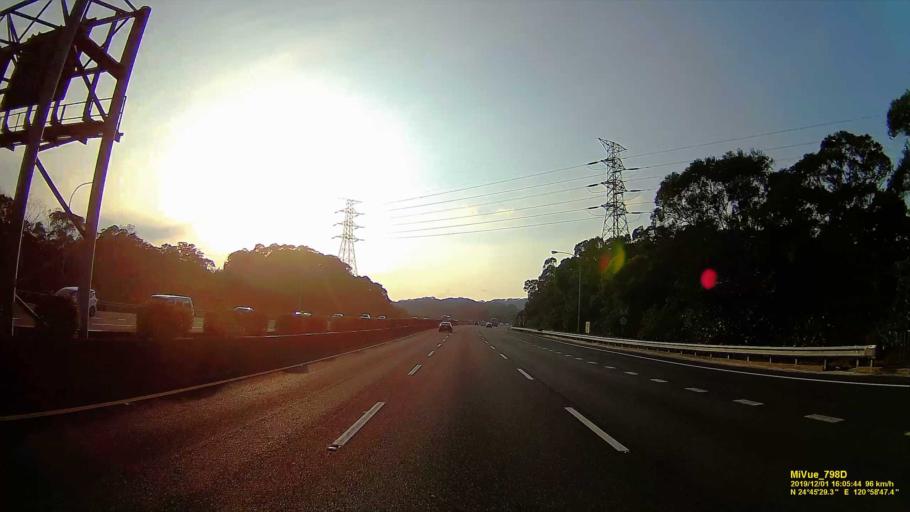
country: TW
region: Taiwan
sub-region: Hsinchu
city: Hsinchu
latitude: 24.7568
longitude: 120.9767
